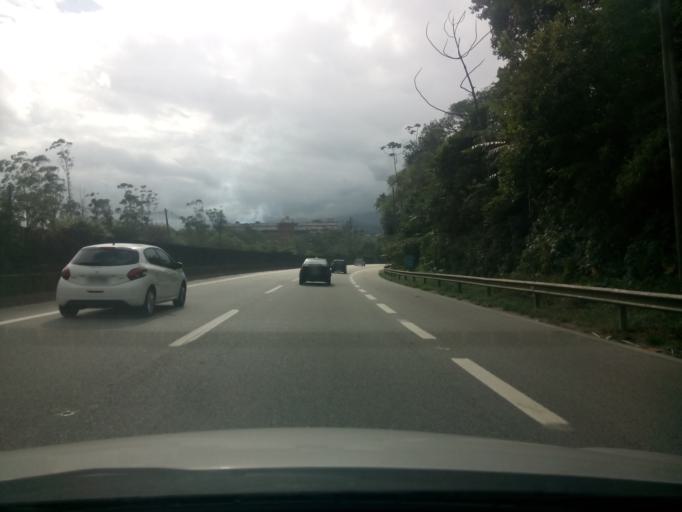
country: BR
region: Sao Paulo
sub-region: Cubatao
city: Cubatao
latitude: -23.8575
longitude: -46.3657
